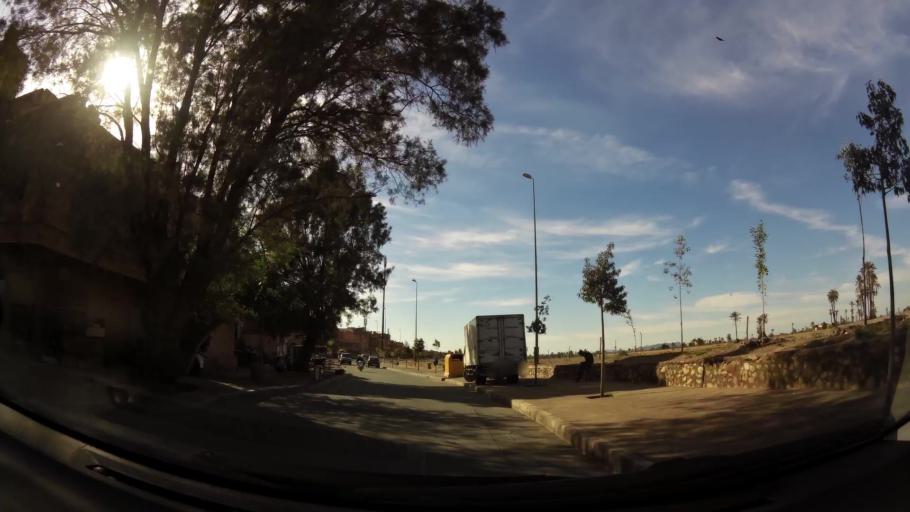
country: MA
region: Marrakech-Tensift-Al Haouz
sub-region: Marrakech
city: Marrakesh
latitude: 31.6147
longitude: -7.9609
